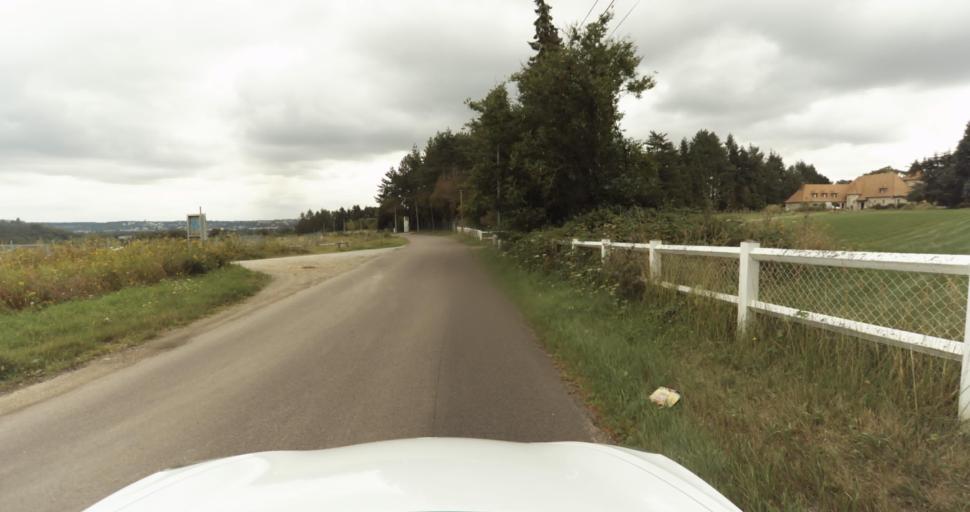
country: FR
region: Haute-Normandie
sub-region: Departement de l'Eure
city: Saint-Sebastien-de-Morsent
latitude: 49.0173
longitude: 1.1008
